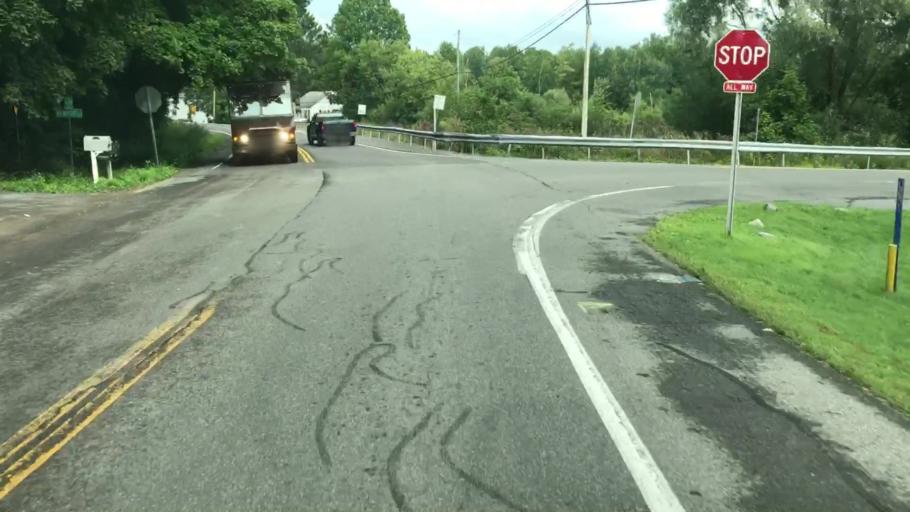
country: US
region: New York
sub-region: Onondaga County
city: Camillus
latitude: 43.0740
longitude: -76.3292
